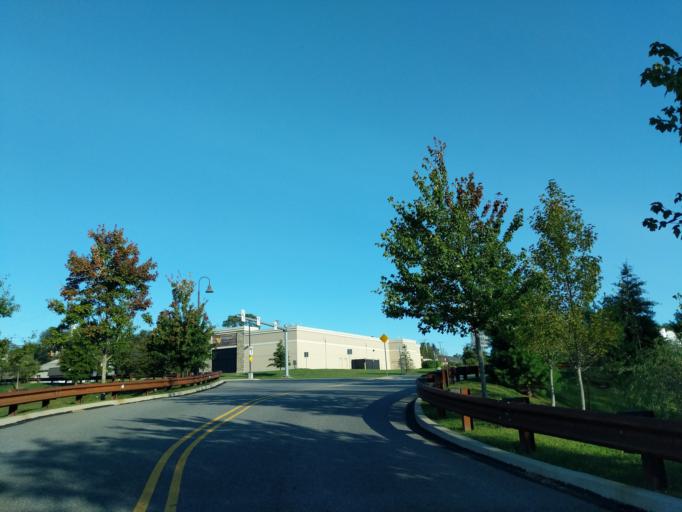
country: US
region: Pennsylvania
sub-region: Delaware County
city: Chester Heights
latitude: 39.8754
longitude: -75.5438
